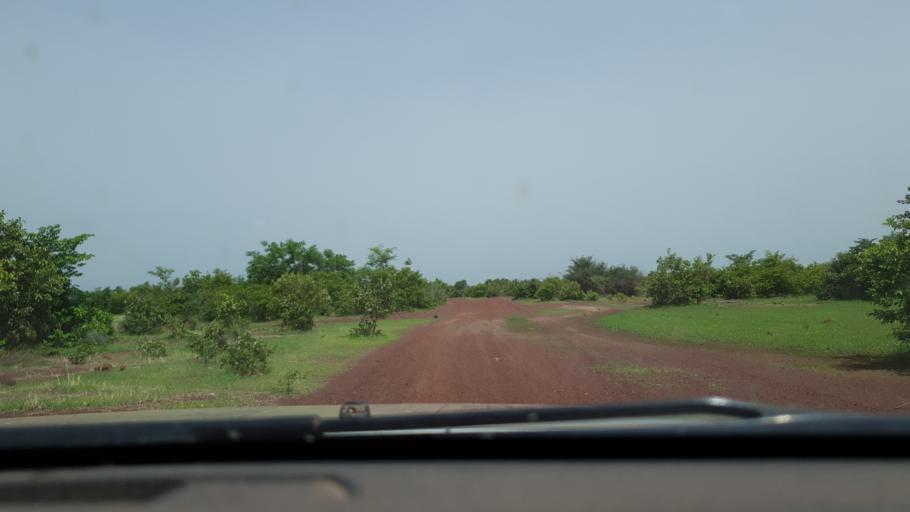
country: ML
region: Koulikoro
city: Koulikoro
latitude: 12.6662
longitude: -7.2326
